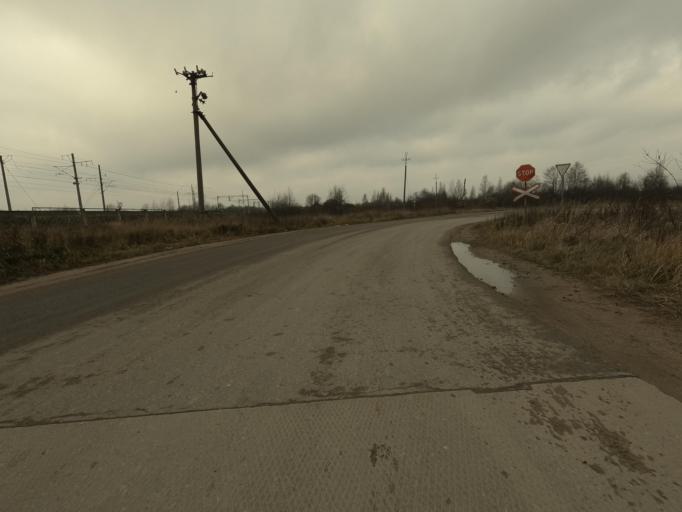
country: RU
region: Leningrad
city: Lyuban'
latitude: 59.4795
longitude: 31.2592
